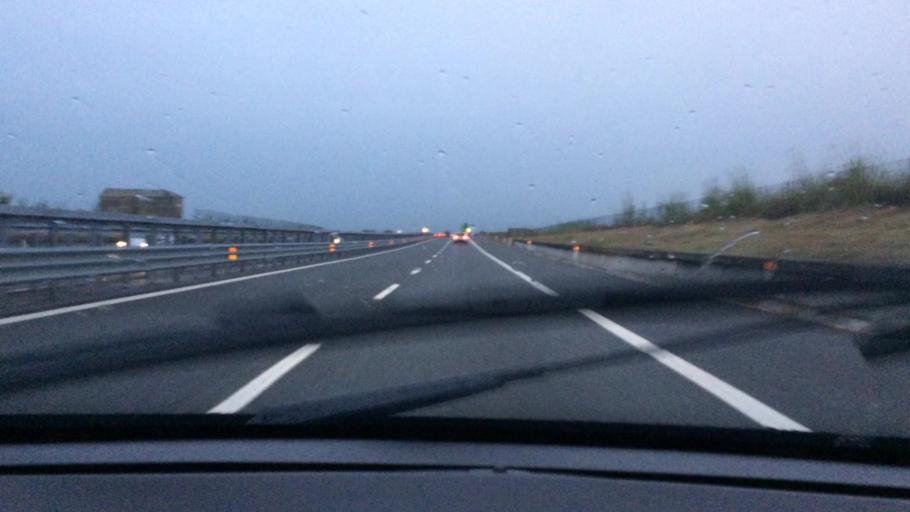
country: IT
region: Piedmont
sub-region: Provincia di Torino
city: Pasta
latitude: 44.9950
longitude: 7.5623
